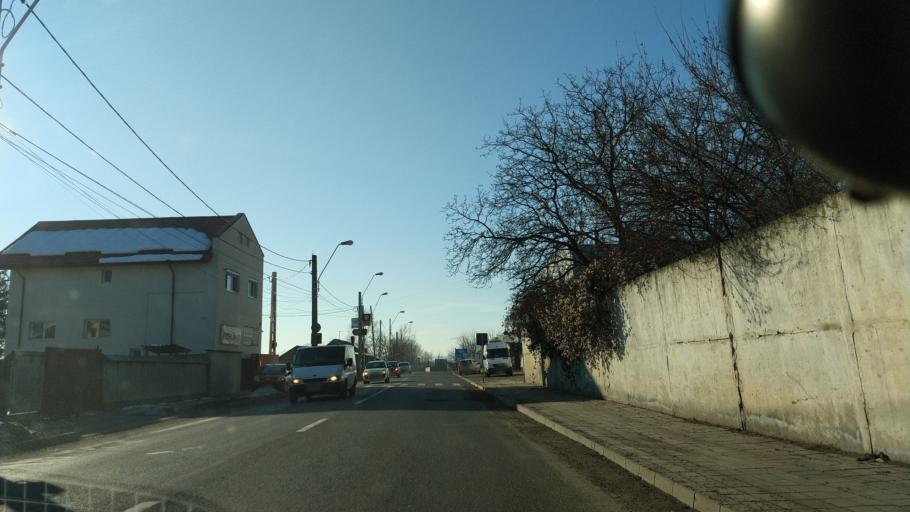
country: RO
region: Neamt
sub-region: Municipiul Roman
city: Roman
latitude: 46.9278
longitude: 26.9113
